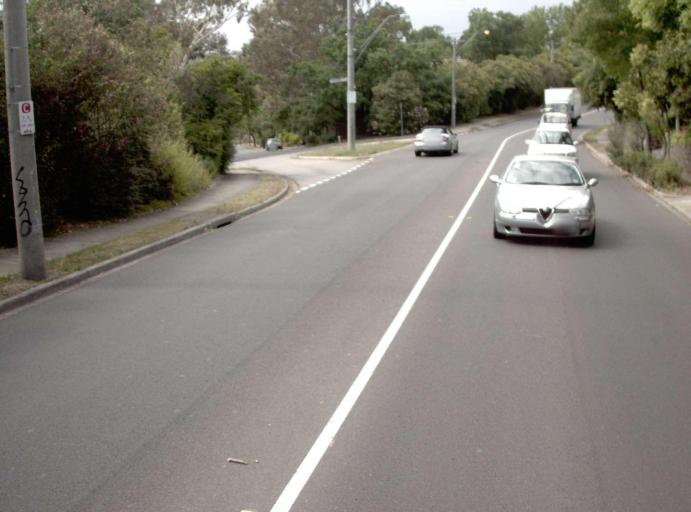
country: AU
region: Victoria
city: Ivanhoe East
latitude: -37.7713
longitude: 145.0640
